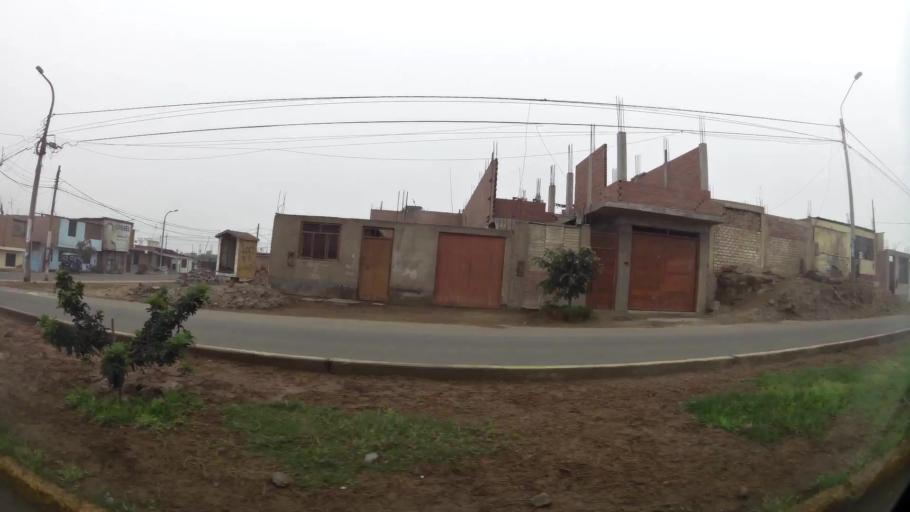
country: PE
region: Lima
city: Ventanilla
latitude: -11.8305
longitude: -77.1052
